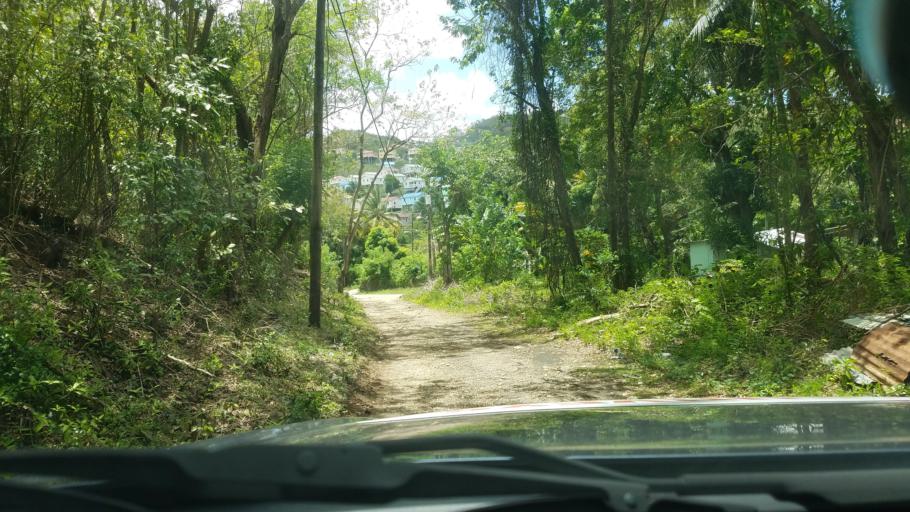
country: LC
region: Gros-Islet
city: Gros Islet
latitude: 14.0552
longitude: -60.9272
